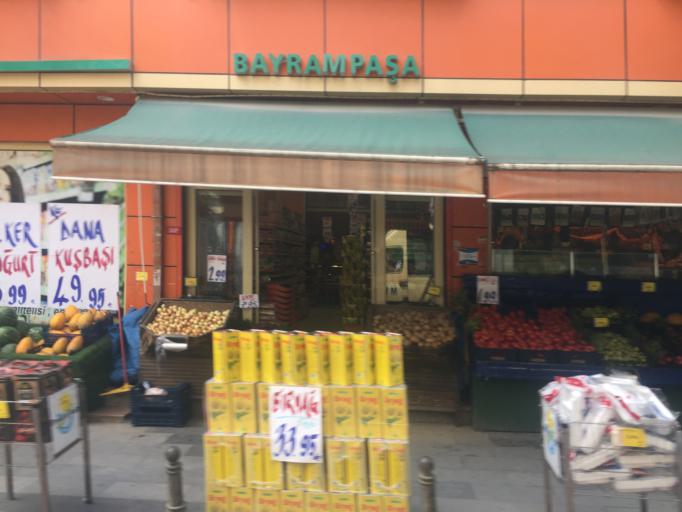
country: TR
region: Istanbul
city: Esenler
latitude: 41.0499
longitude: 28.9066
